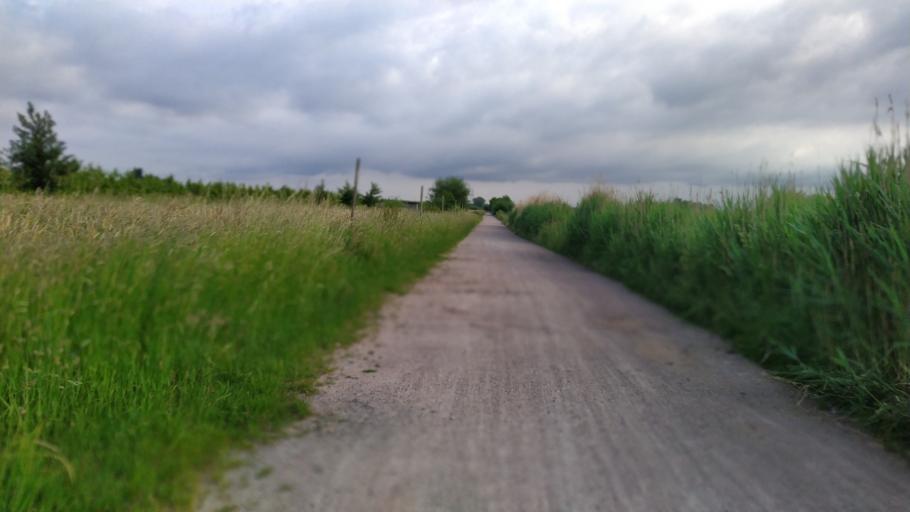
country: DE
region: Lower Saxony
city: Neu Wulmstorf
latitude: 53.5068
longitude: 9.8087
